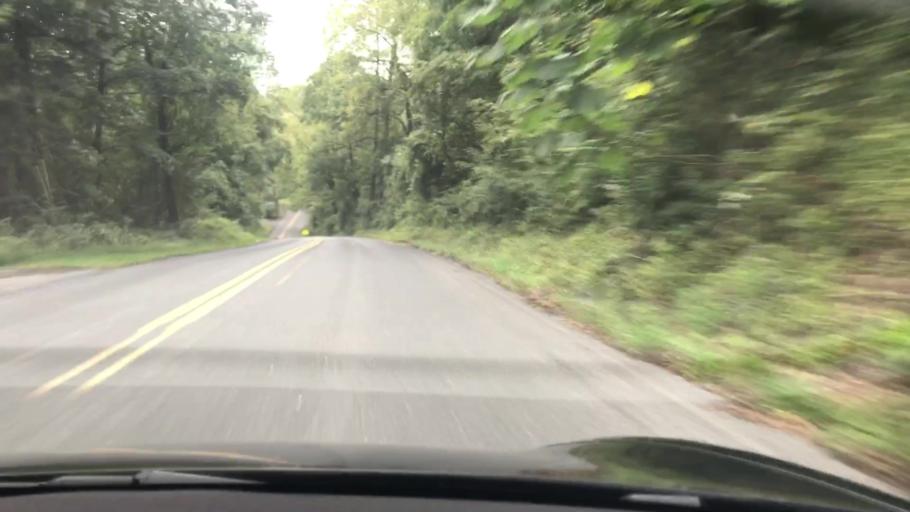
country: US
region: Pennsylvania
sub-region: York County
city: Dillsburg
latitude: 40.1115
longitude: -76.9727
